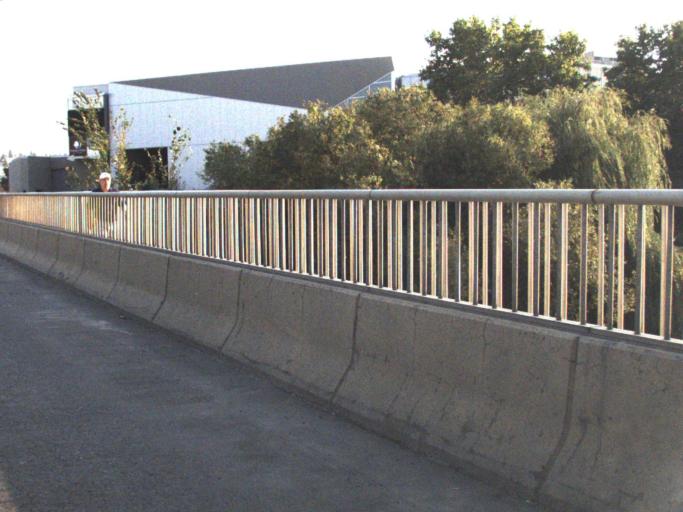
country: US
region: Washington
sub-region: Spokane County
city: Spokane
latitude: 47.6621
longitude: -117.4112
